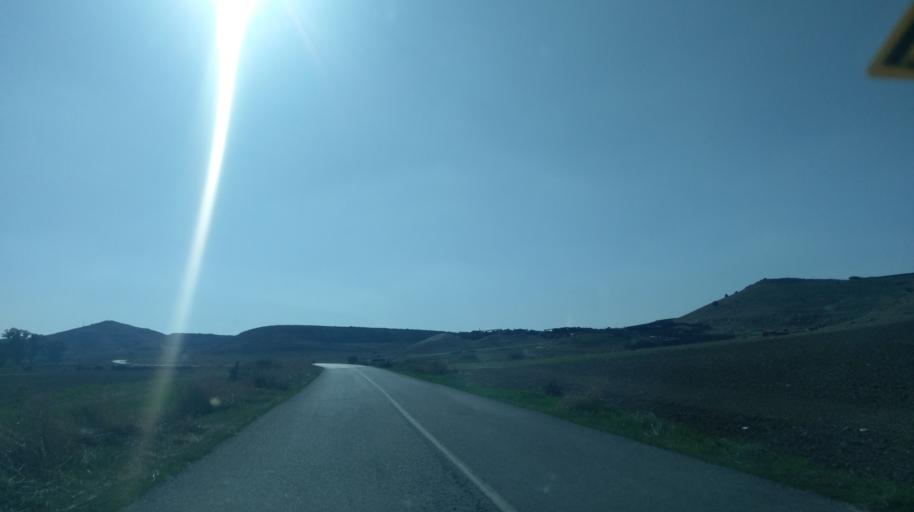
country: CY
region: Lefkosia
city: Lympia
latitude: 35.0556
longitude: 33.4806
